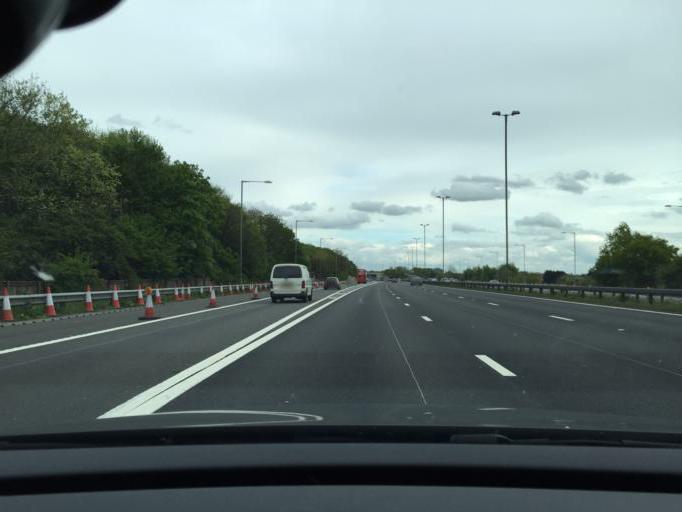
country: GB
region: England
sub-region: Wokingham
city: Shinfield
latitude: 51.4159
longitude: -0.9821
